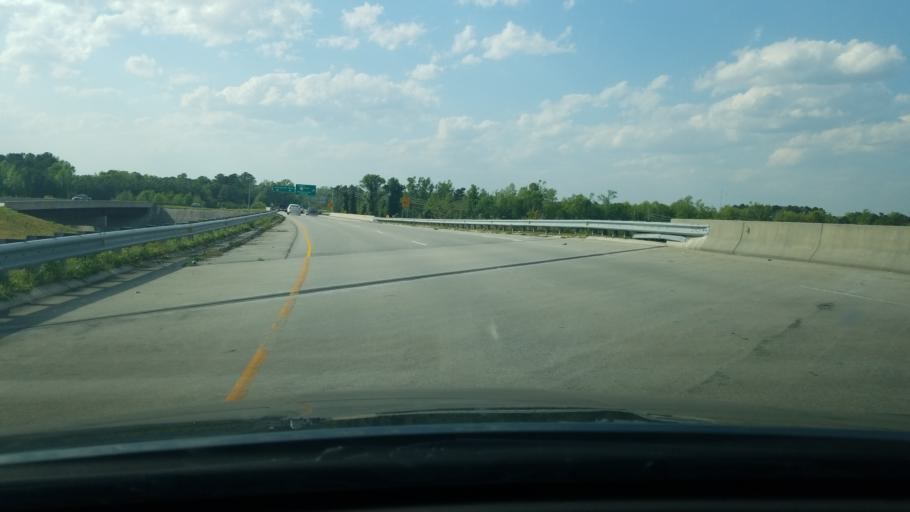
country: US
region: North Carolina
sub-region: Onslow County
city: Pumpkin Center
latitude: 34.7726
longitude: -77.3971
